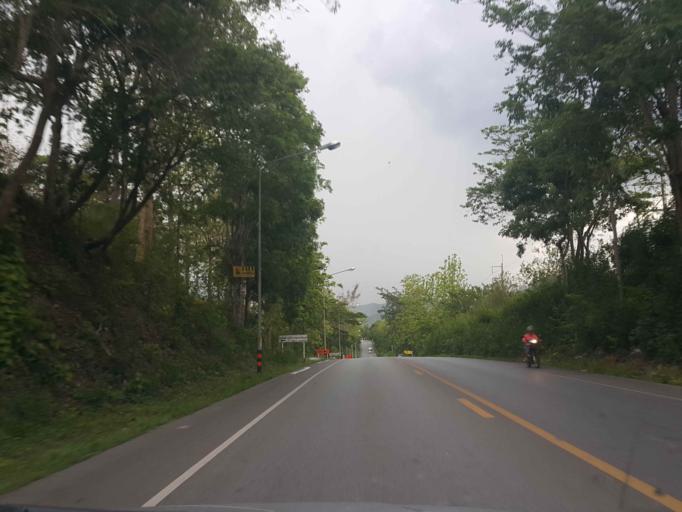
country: TH
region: Phrae
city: Den Chai
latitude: 17.9731
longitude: 100.0426
